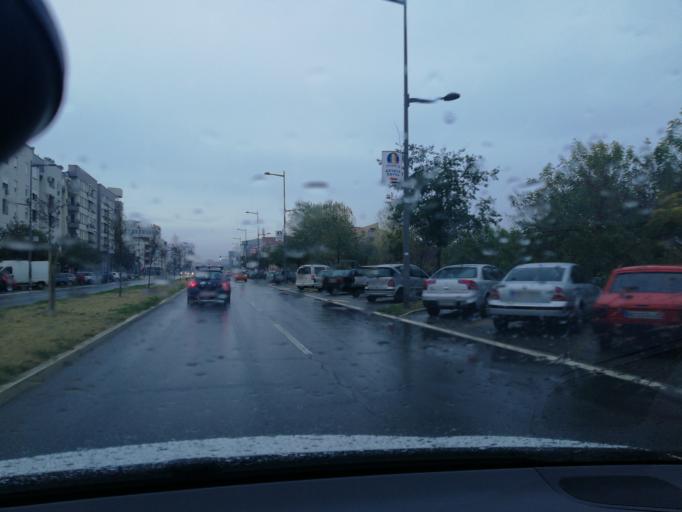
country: RS
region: Autonomna Pokrajina Vojvodina
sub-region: Juznobacki Okrug
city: Novi Sad
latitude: 45.2405
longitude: 19.8139
